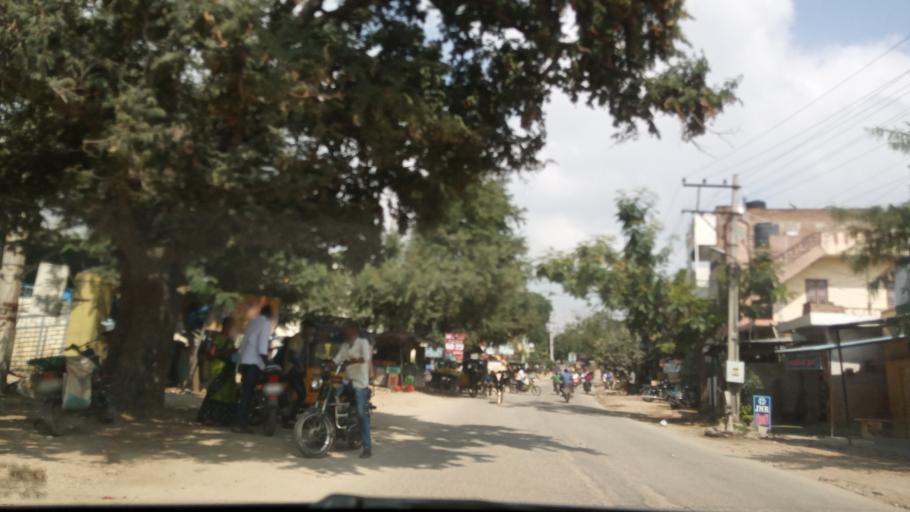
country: IN
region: Andhra Pradesh
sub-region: Chittoor
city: Madanapalle
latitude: 13.5644
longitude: 78.5123
